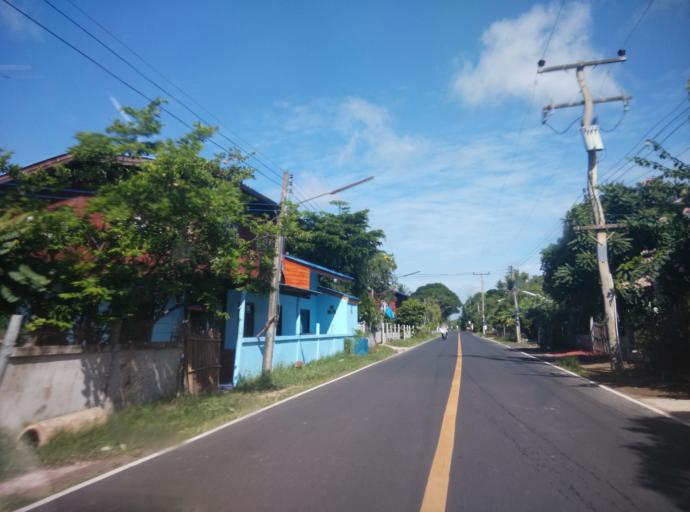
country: TH
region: Sisaket
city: Uthumphon Phisai
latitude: 15.1242
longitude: 104.2001
